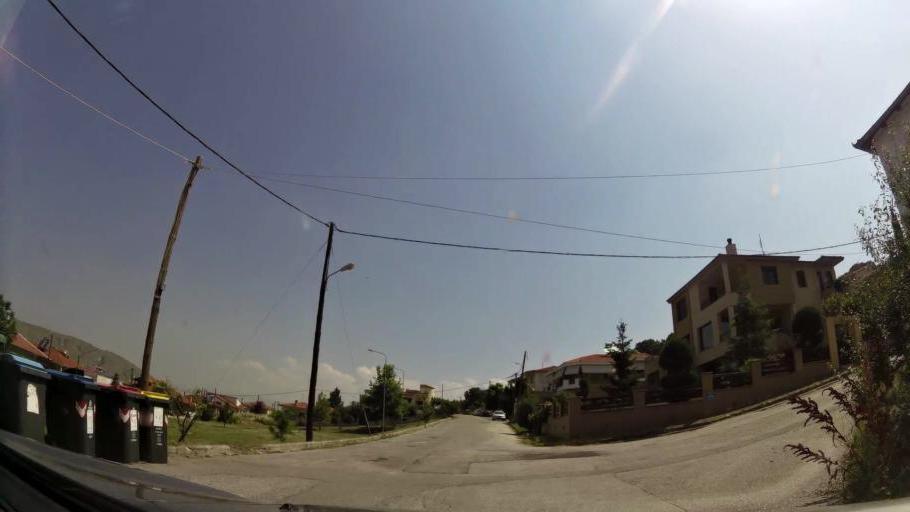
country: GR
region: West Macedonia
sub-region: Nomos Kozanis
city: Koila
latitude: 40.3261
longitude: 21.7927
